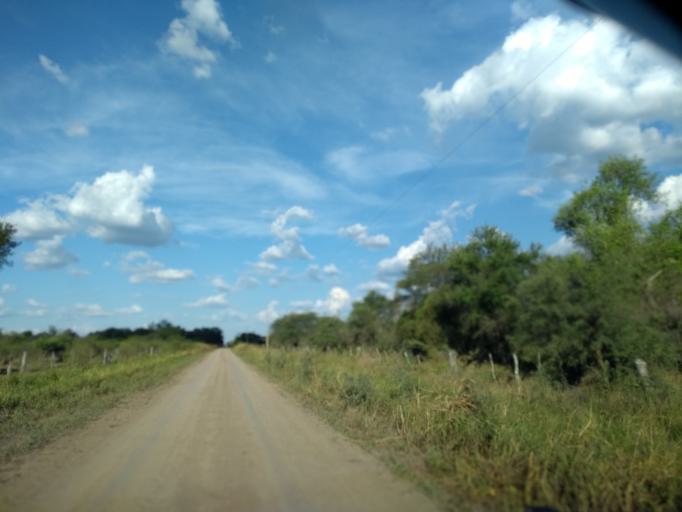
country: AR
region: Chaco
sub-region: Departamento de Quitilipi
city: Quitilipi
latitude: -26.7468
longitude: -60.2721
